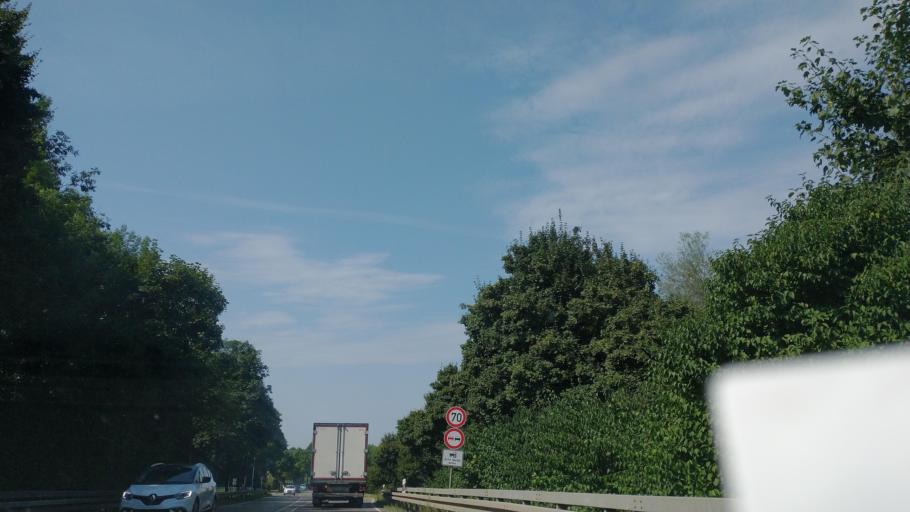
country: DE
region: Baden-Wuerttemberg
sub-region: Tuebingen Region
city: Tettnang
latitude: 47.6667
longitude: 9.5778
